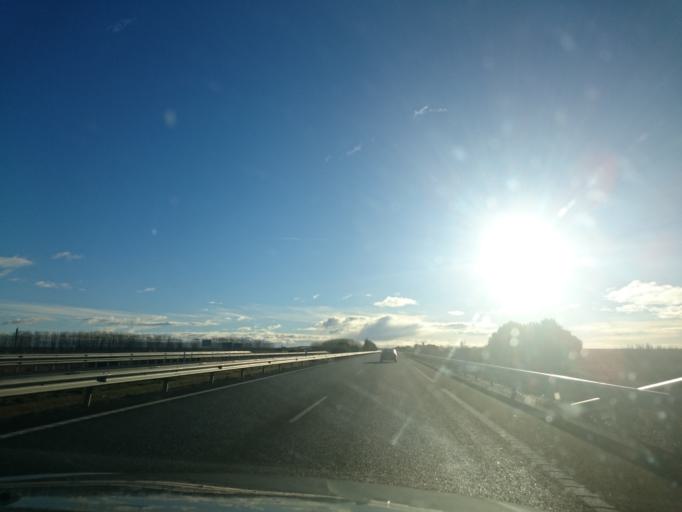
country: ES
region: Castille and Leon
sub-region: Provincia de Leon
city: Bercianos del Real Camino
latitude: 42.4028
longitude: -5.1719
